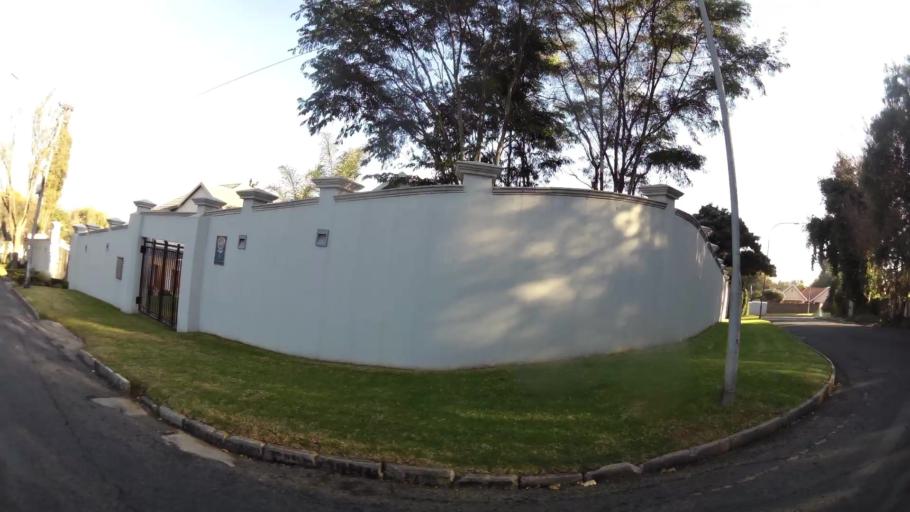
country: ZA
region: Gauteng
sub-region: City of Johannesburg Metropolitan Municipality
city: Johannesburg
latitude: -26.1294
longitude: 28.0772
